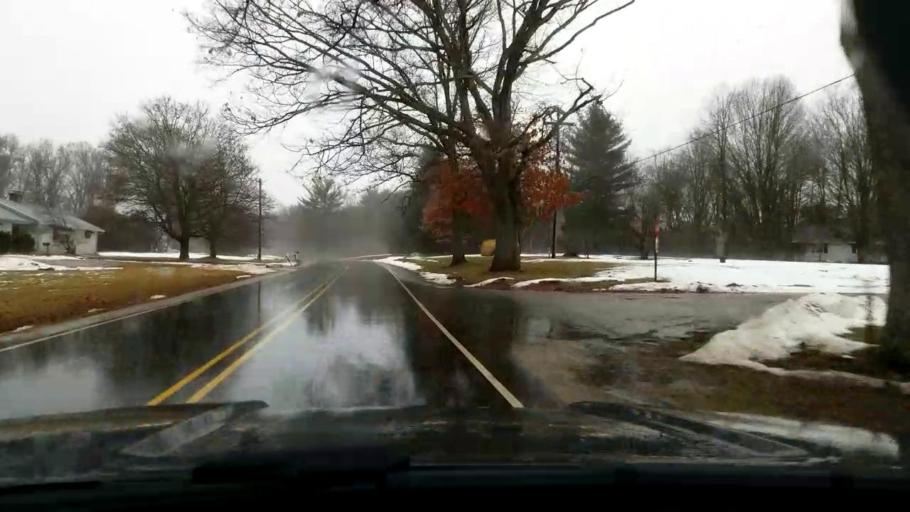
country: US
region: Michigan
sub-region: Jackson County
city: Michigan Center
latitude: 42.2884
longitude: -84.3255
